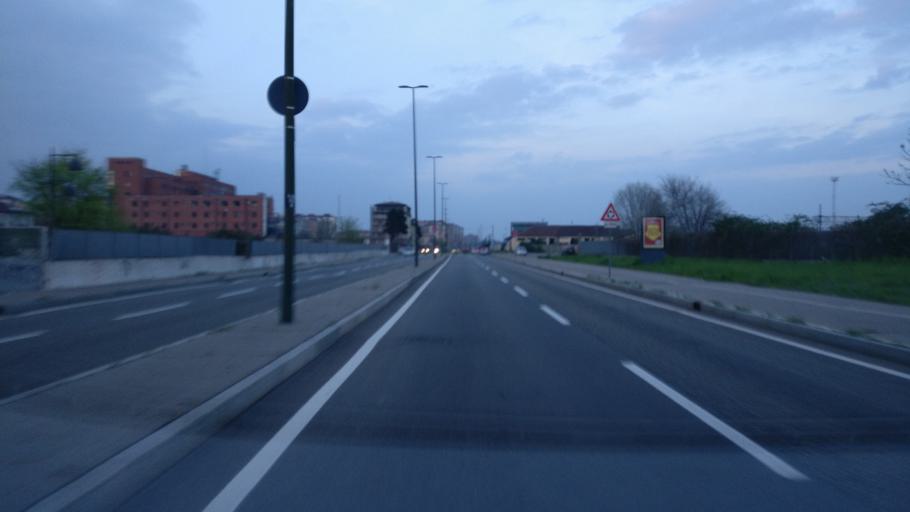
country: IT
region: Piedmont
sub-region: Provincia di Torino
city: Nichelino
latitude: 45.0330
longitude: 7.6586
